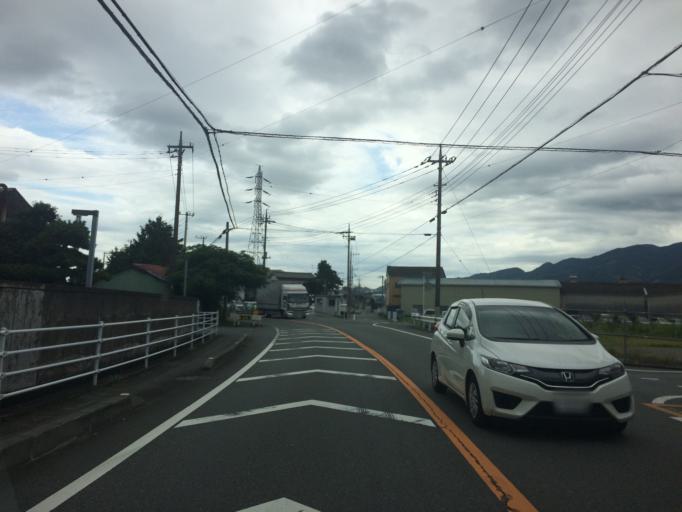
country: JP
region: Shizuoka
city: Fuji
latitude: 35.1817
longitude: 138.6477
